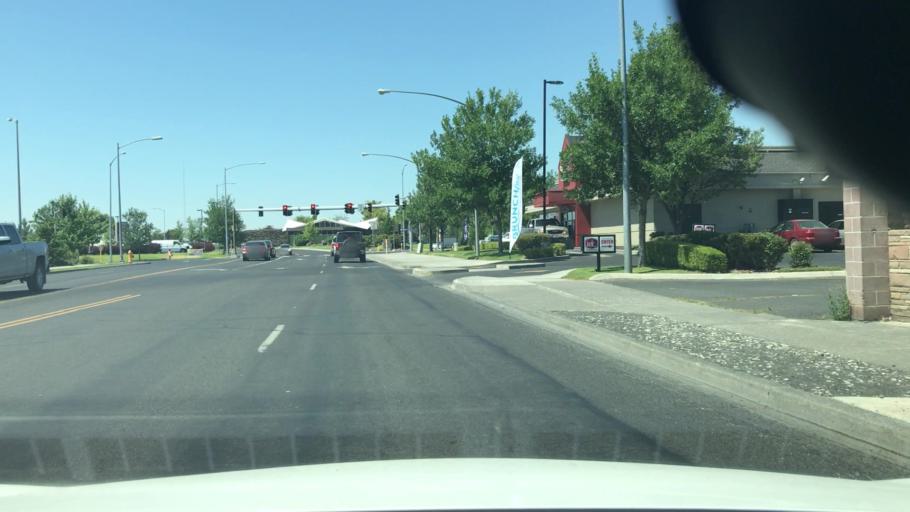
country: US
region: Washington
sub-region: Grant County
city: Moses Lake
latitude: 47.1312
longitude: -119.2690
